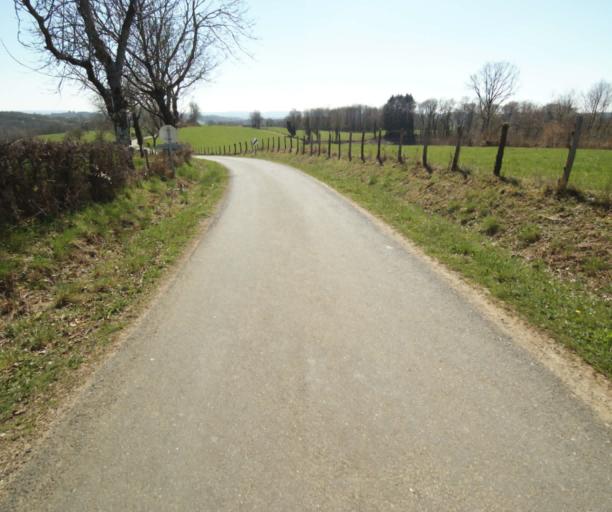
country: FR
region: Limousin
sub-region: Departement de la Correze
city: Saint-Clement
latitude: 45.3332
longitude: 1.7072
